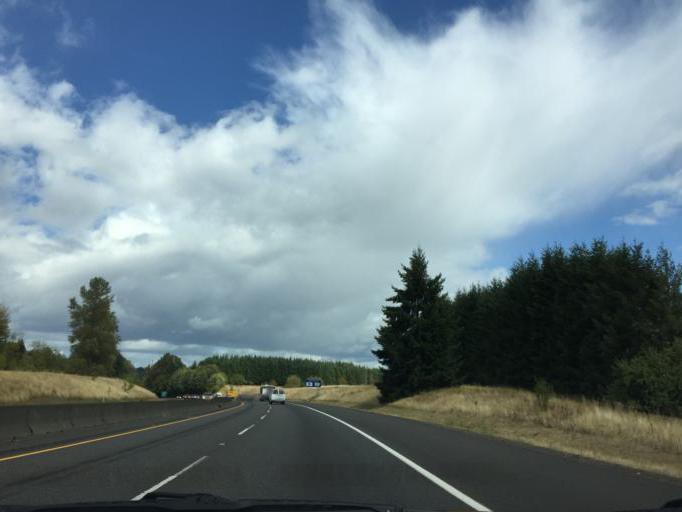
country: US
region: Washington
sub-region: Lewis County
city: Winlock
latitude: 46.4077
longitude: -122.8898
